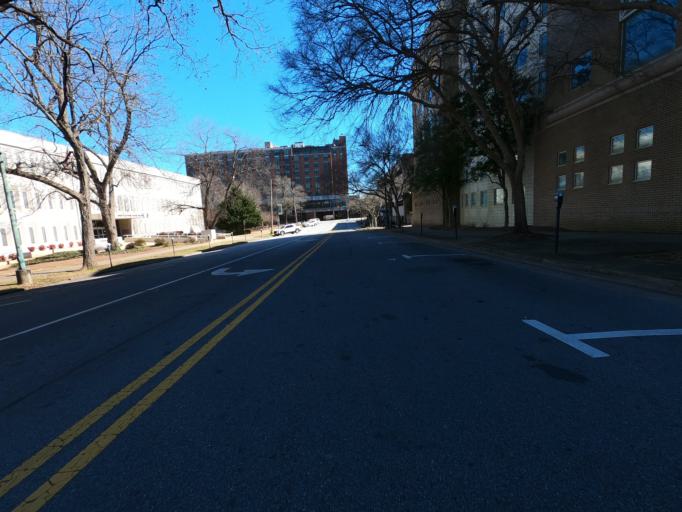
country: US
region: Georgia
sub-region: Clarke County
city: Athens
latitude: 33.9604
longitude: -83.3749
